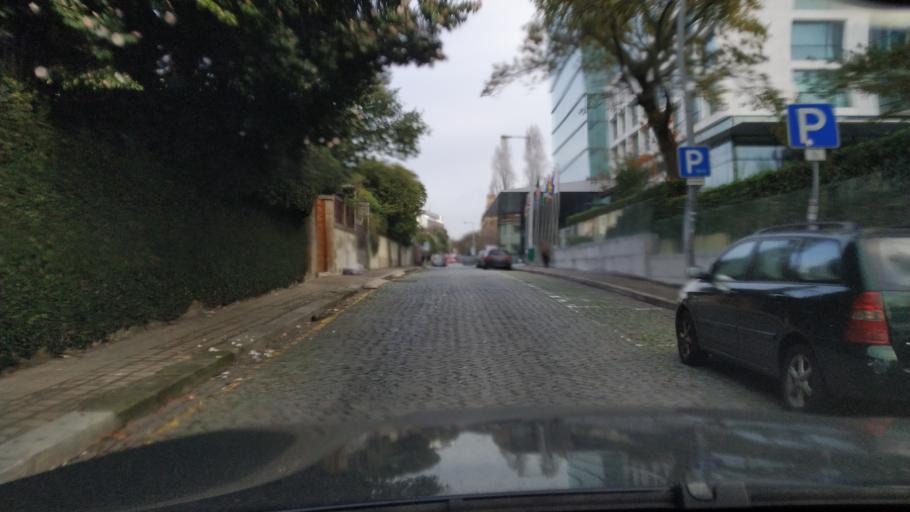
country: PT
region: Porto
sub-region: Matosinhos
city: Senhora da Hora
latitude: 41.1607
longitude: -8.6413
